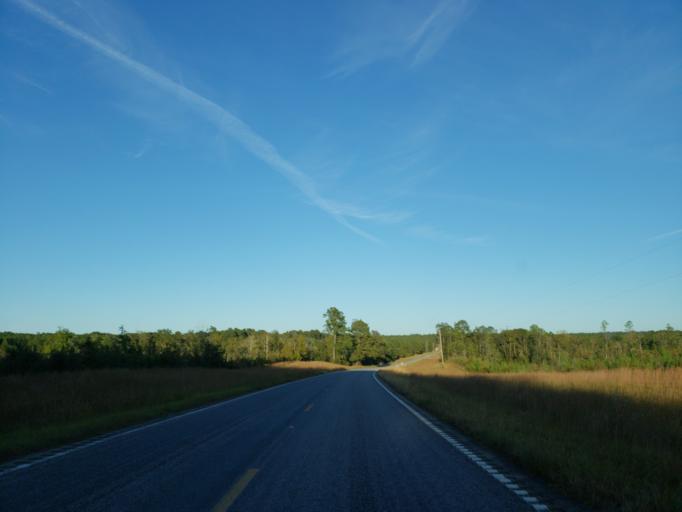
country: US
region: Mississippi
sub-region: Wayne County
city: Belmont
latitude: 31.4091
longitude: -88.6120
